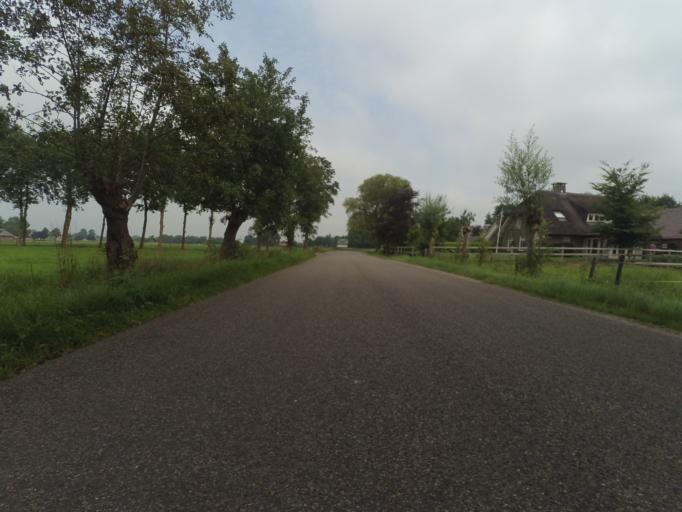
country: NL
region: Gelderland
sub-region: Gemeente Ede
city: Lunteren
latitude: 52.1137
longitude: 5.6345
